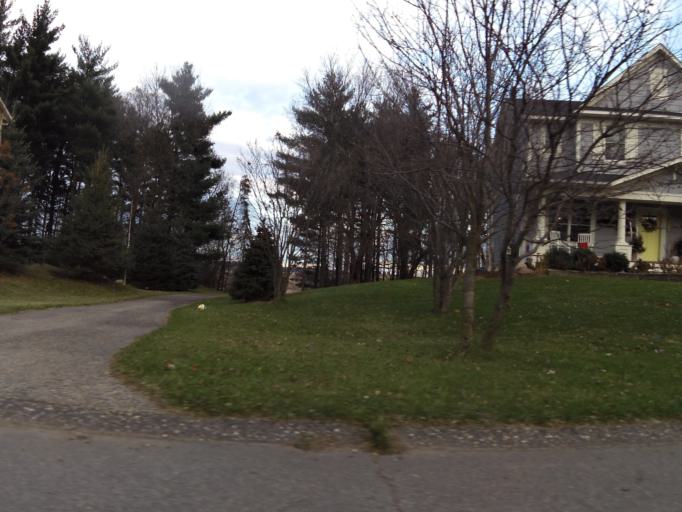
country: US
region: Minnesota
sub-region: Washington County
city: Bayport
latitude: 45.0057
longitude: -92.7973
